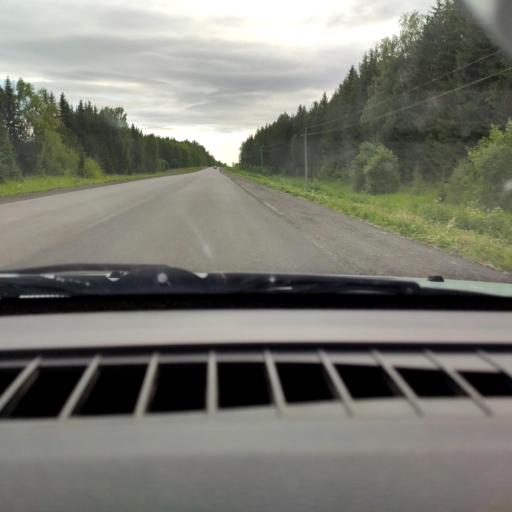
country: RU
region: Perm
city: Orda
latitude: 57.2203
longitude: 56.9500
